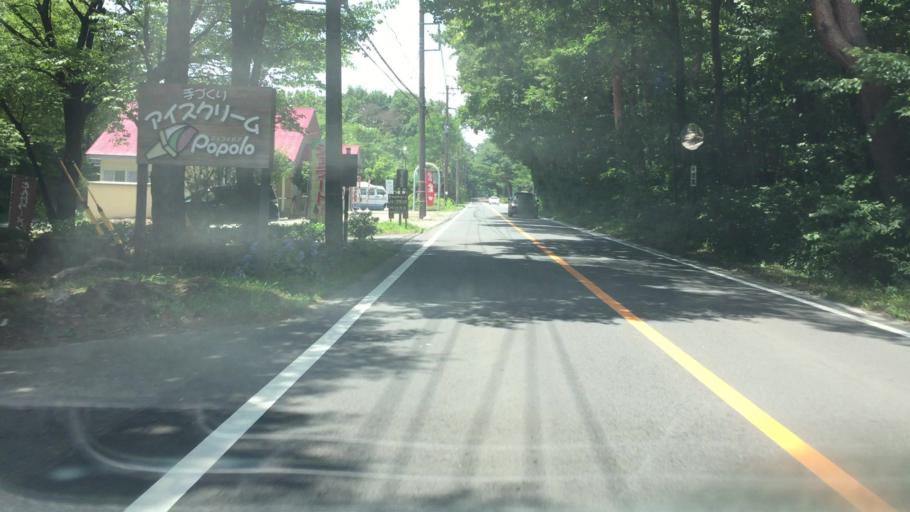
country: JP
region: Tochigi
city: Kuroiso
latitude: 37.0292
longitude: 139.9847
